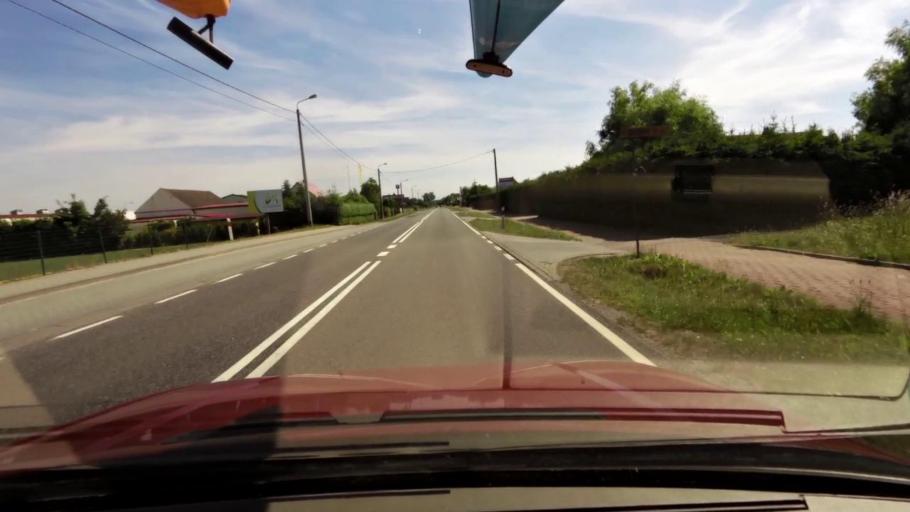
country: PL
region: Pomeranian Voivodeship
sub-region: Powiat slupski
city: Kobylnica
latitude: 54.4186
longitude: 17.0075
